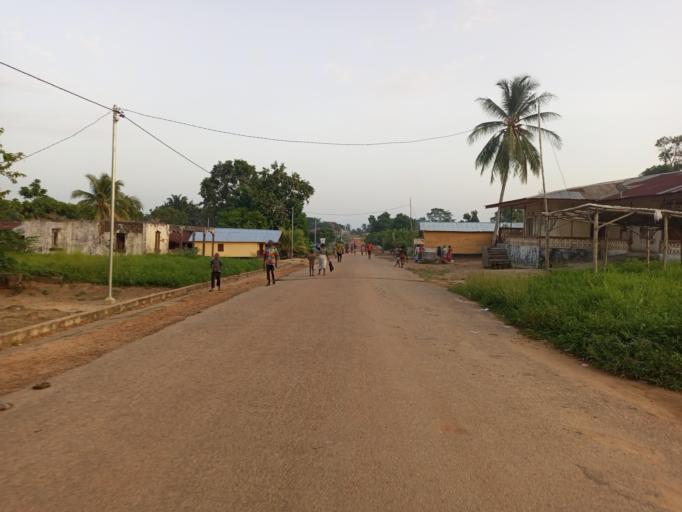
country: SL
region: Eastern Province
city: Pendembu
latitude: 8.0953
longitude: -10.6937
